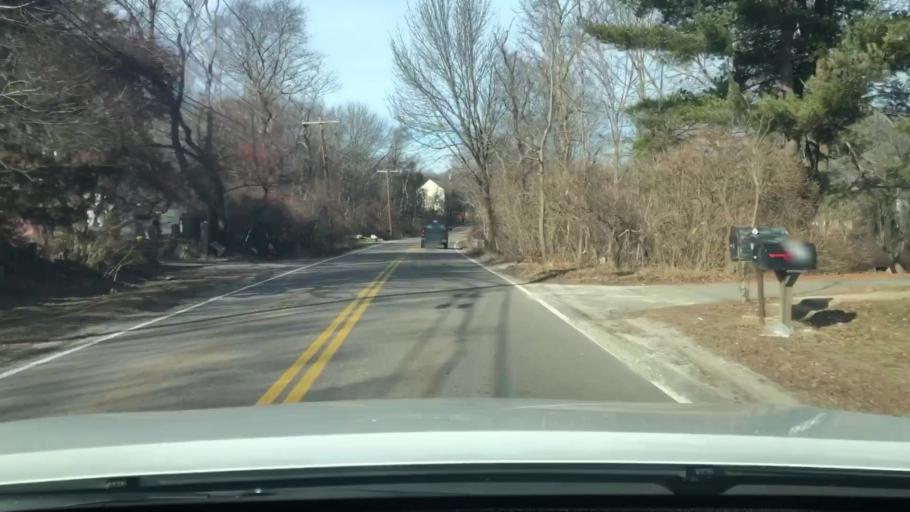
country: US
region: Massachusetts
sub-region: Worcester County
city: Blackstone
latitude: 42.0589
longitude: -71.5258
